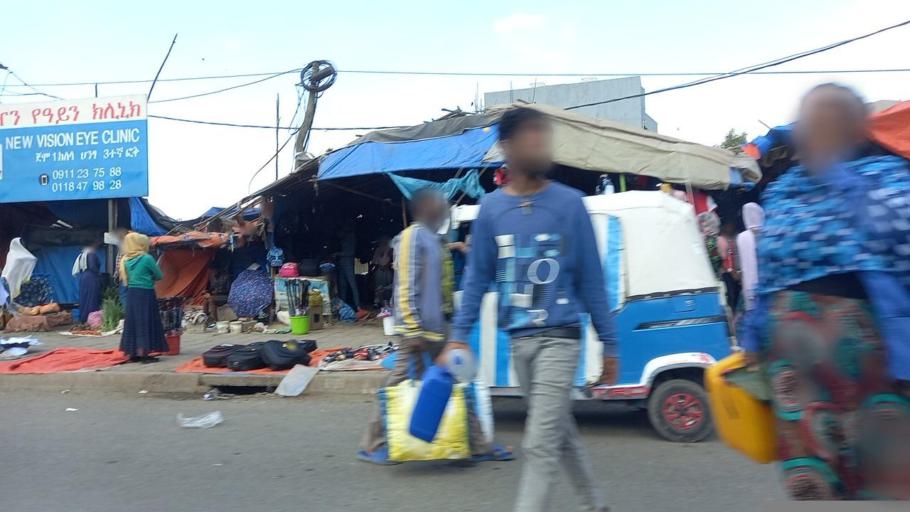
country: ET
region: Adis Abeba
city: Addis Ababa
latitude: 8.9605
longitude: 38.7120
